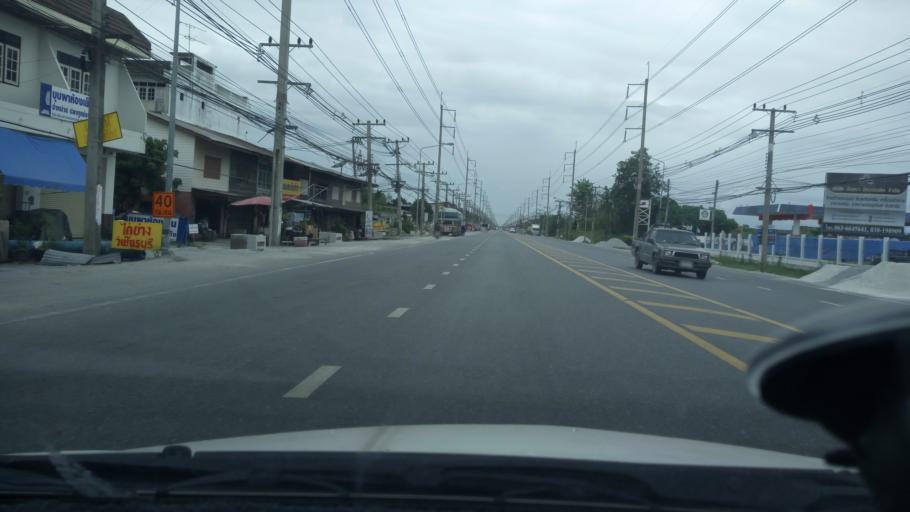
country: TH
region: Chon Buri
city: Phanat Nikhom
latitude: 13.4639
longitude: 101.1724
